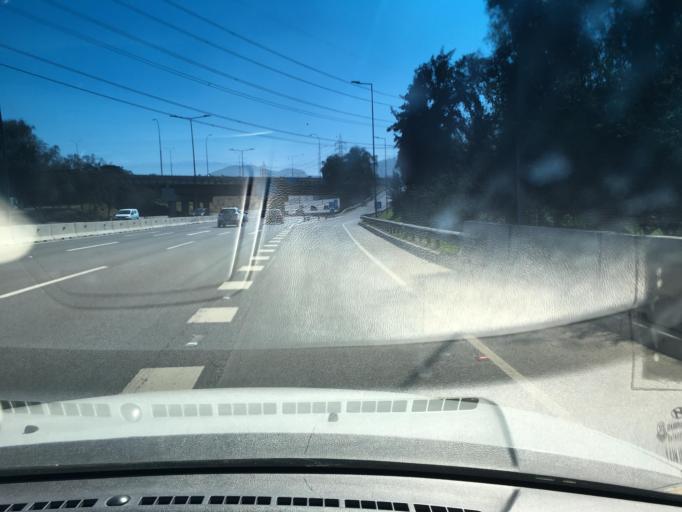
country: CL
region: Santiago Metropolitan
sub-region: Provincia de Santiago
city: Lo Prado
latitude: -33.4183
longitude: -70.6882
